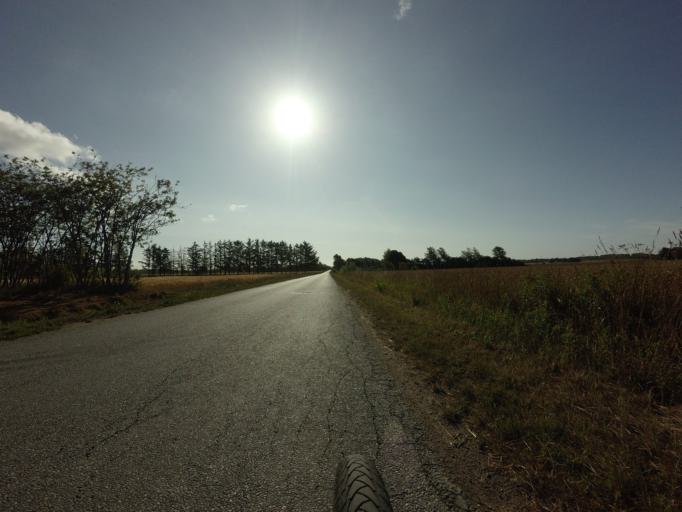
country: DK
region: North Denmark
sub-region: Hjorring Kommune
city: Vra
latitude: 57.3937
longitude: 9.9590
